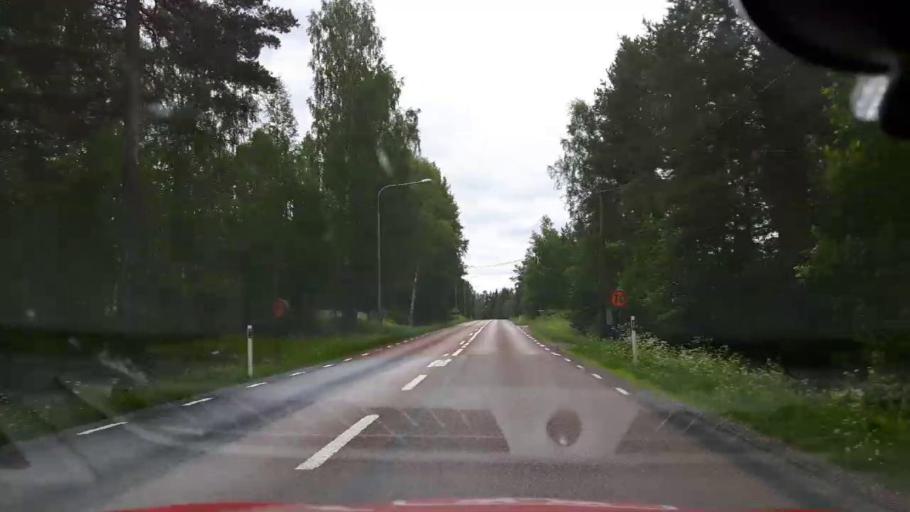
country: SE
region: Jaemtland
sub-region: OEstersunds Kommun
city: Brunflo
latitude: 62.9523
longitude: 15.0483
